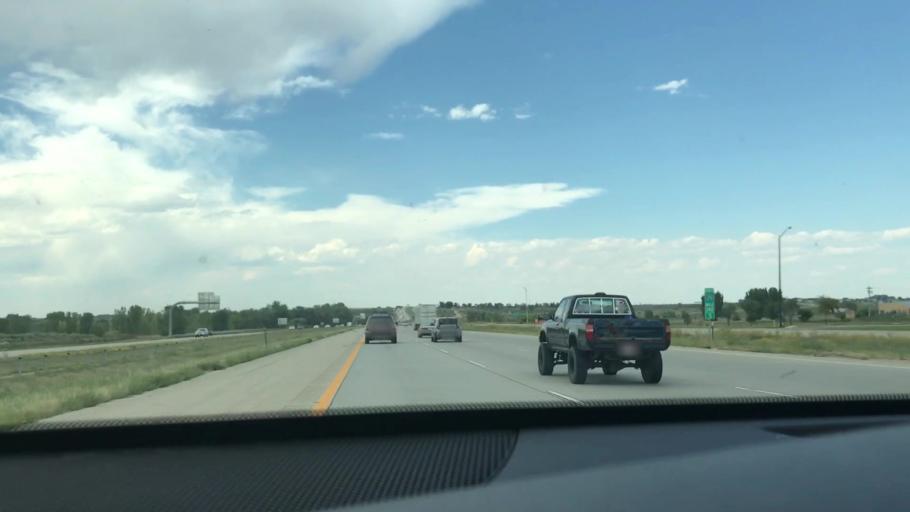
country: US
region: Colorado
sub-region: Weld County
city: Firestone
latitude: 40.1653
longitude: -104.9788
